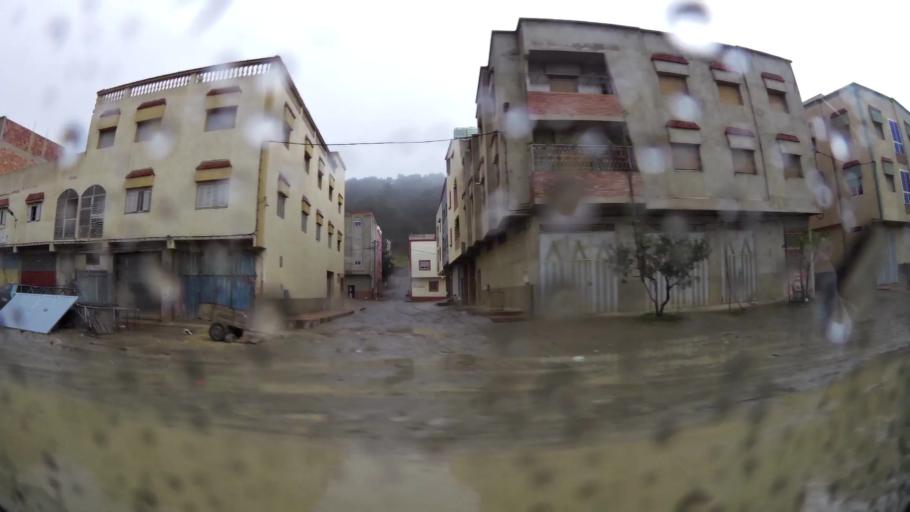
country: MA
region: Taza-Al Hoceima-Taounate
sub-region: Taza
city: Aknoul
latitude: 34.7607
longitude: -3.7969
